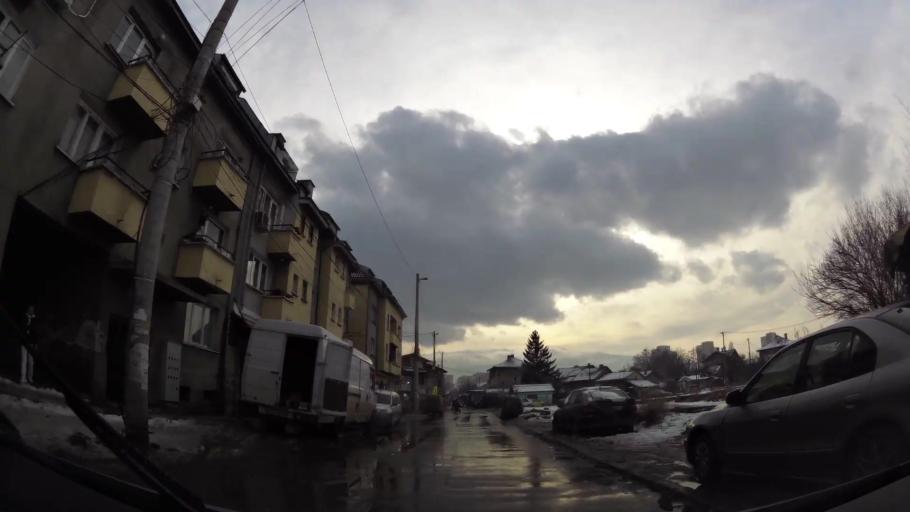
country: BG
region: Sofia-Capital
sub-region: Stolichna Obshtina
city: Sofia
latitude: 42.6905
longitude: 23.3813
